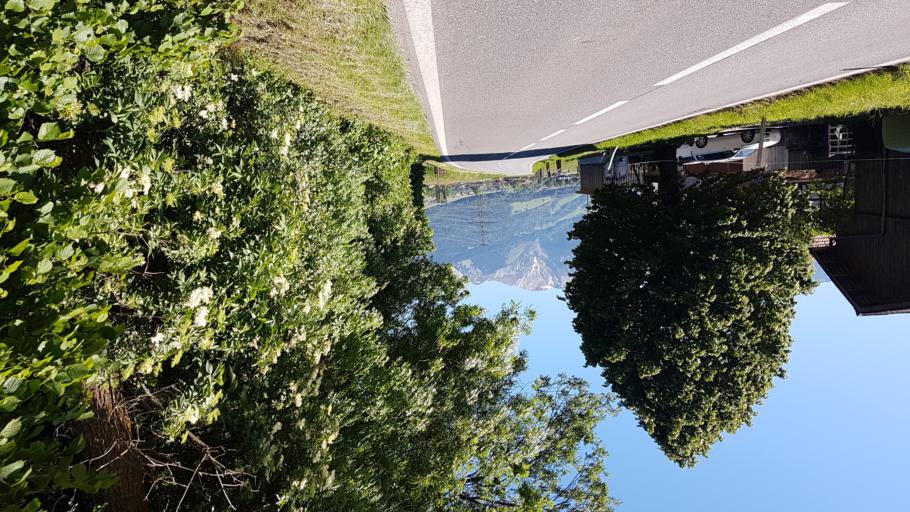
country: CH
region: Bern
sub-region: Thun District
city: Wattenwil
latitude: 46.7804
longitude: 7.5170
